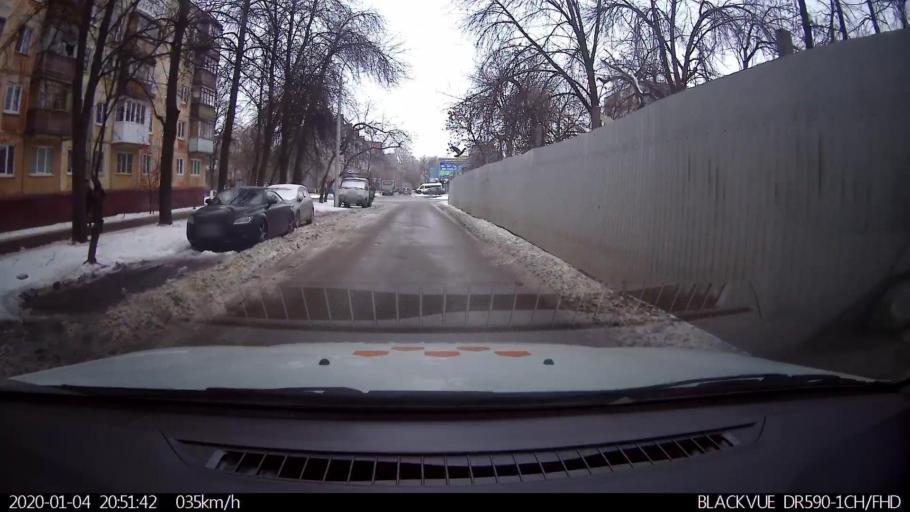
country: RU
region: Nizjnij Novgorod
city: Burevestnik
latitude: 56.2326
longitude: 43.8596
